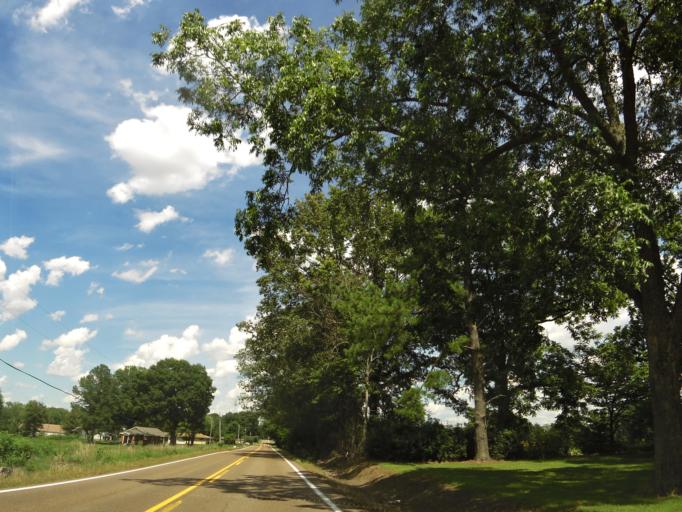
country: US
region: Tennessee
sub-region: Dyer County
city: Newbern
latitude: 36.0285
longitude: -89.2478
